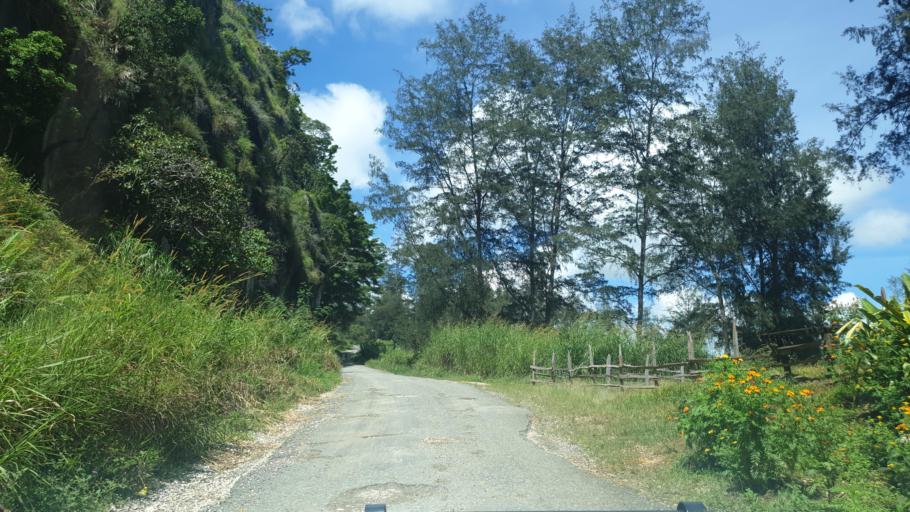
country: PG
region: Chimbu
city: Kundiawa
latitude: -6.1489
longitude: 145.1339
